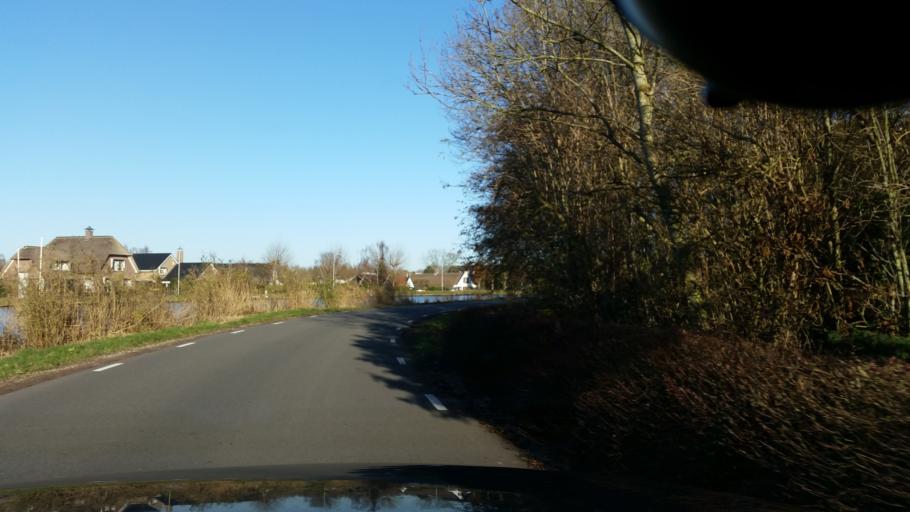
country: NL
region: North Holland
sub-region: Gemeente Ouder-Amstel
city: Ouderkerk aan de Amstel
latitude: 52.2895
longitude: 4.8875
